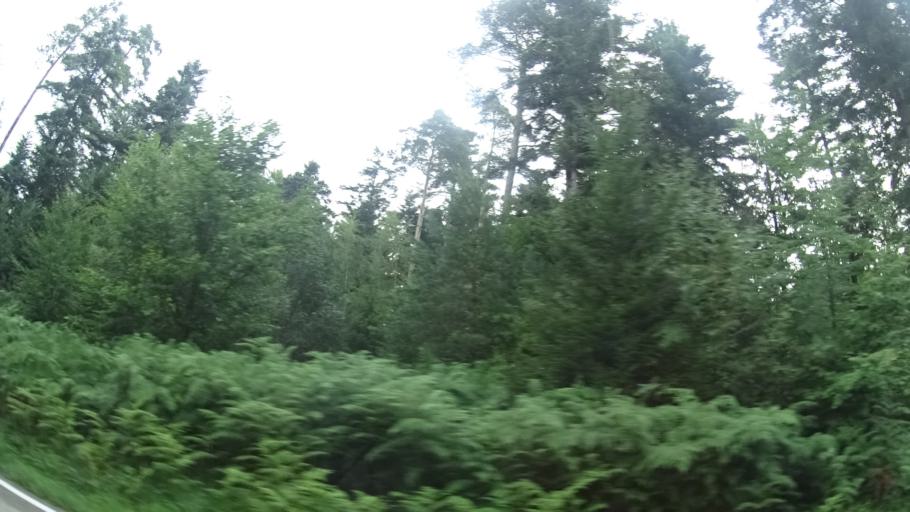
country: DE
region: Baden-Wuerttemberg
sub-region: Karlsruhe Region
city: Dobel
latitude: 48.8116
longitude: 8.4871
